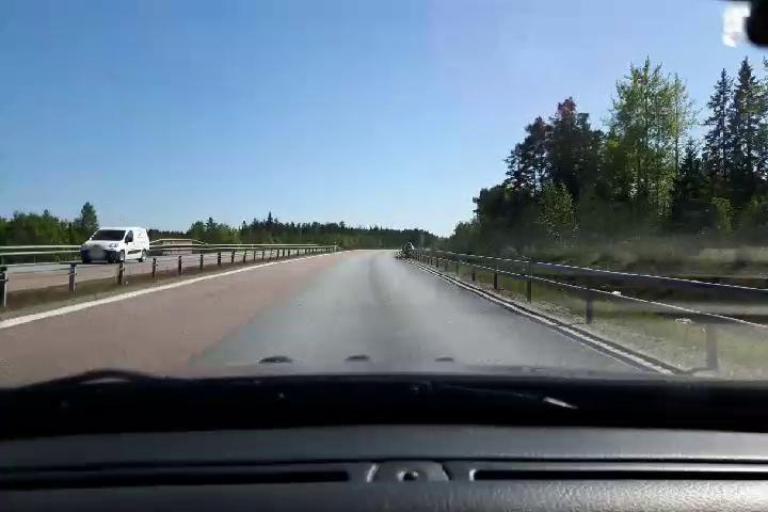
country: SE
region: Gaevleborg
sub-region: Soderhamns Kommun
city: Soderhamn
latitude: 61.3456
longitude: 17.0194
